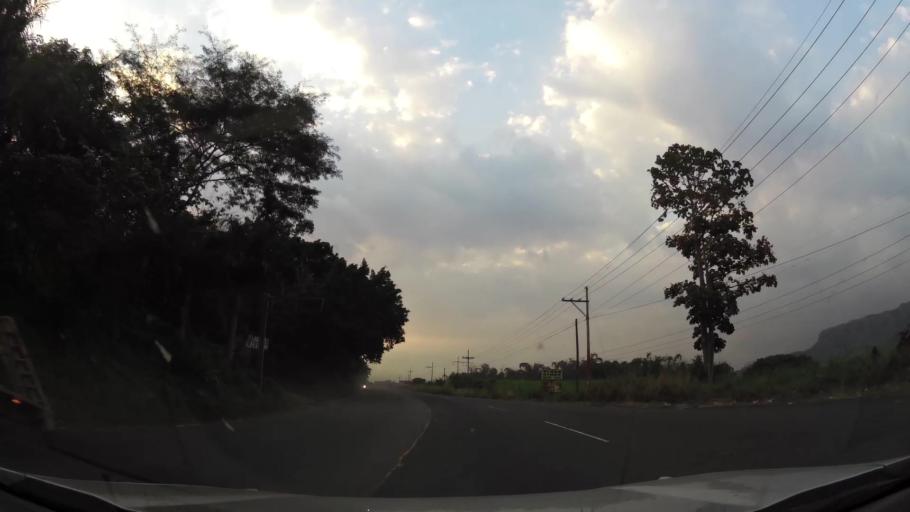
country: GT
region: Escuintla
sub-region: Municipio de La Democracia
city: La Democracia
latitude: 14.2712
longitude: -90.9000
